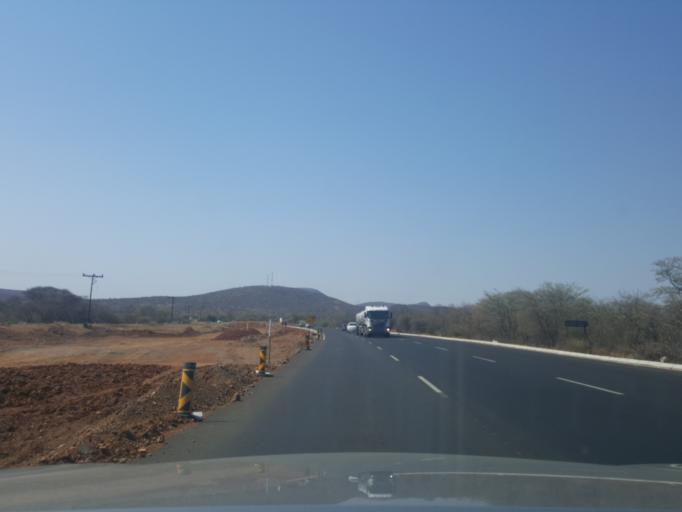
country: BW
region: South East
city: Ramotswa
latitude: -24.7688
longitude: 25.8307
